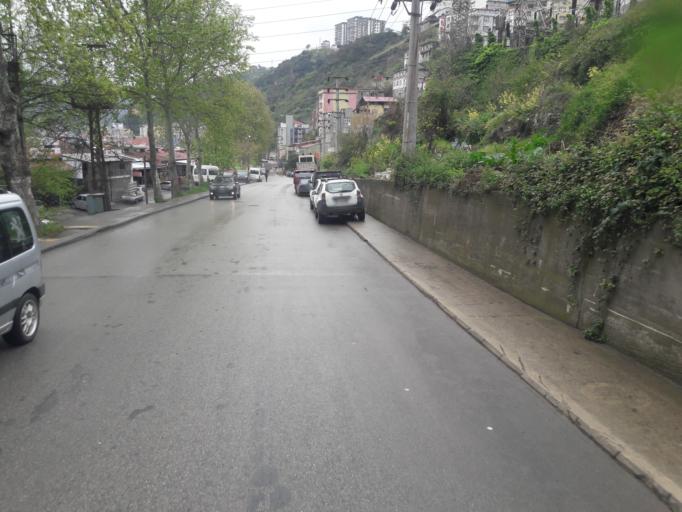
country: TR
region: Trabzon
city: Trabzon
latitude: 40.9933
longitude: 39.7495
